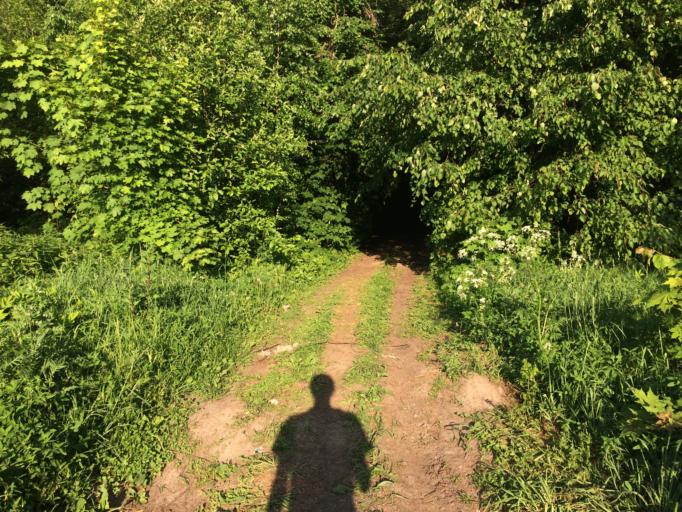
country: RU
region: Mariy-El
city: Mochalishche
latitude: 56.5426
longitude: 48.4115
